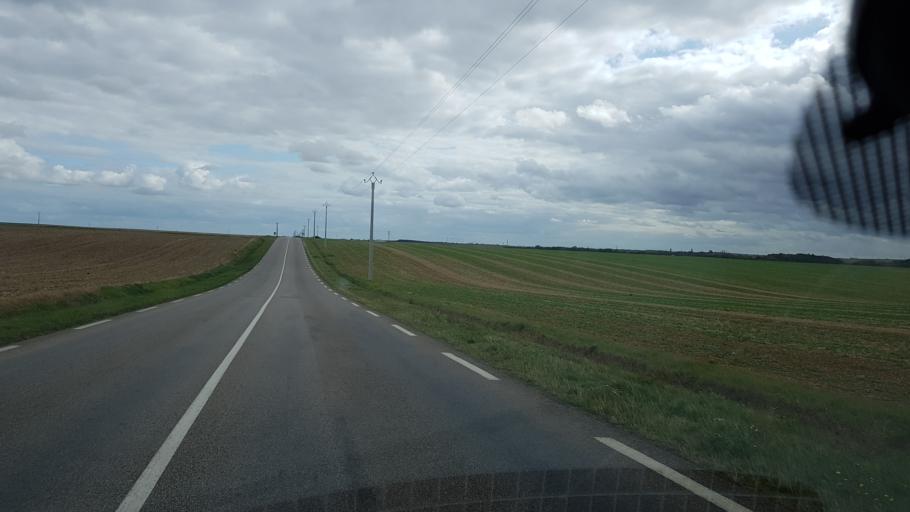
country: FR
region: Ile-de-France
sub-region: Departement de l'Essonne
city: Saclas
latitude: 48.3556
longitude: 2.1692
